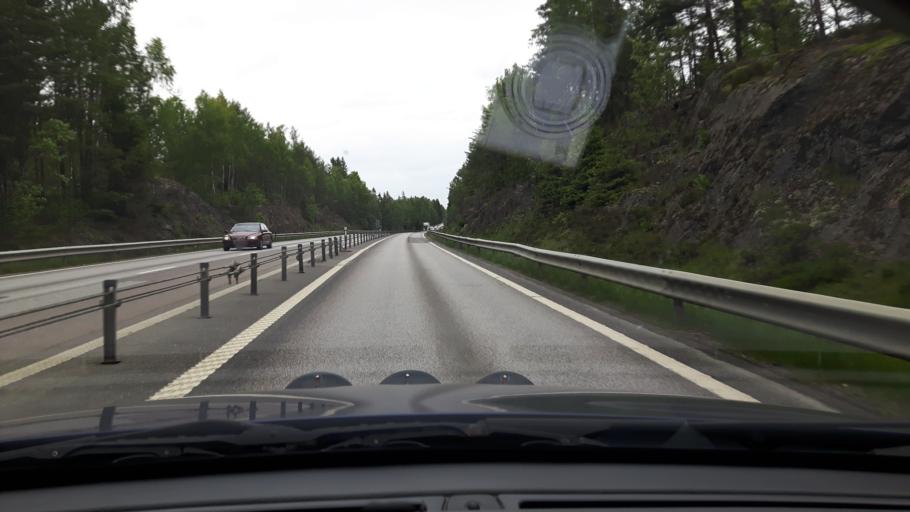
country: SE
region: OEstergoetland
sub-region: Norrkopings Kommun
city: Jursla
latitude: 58.7141
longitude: 16.1634
